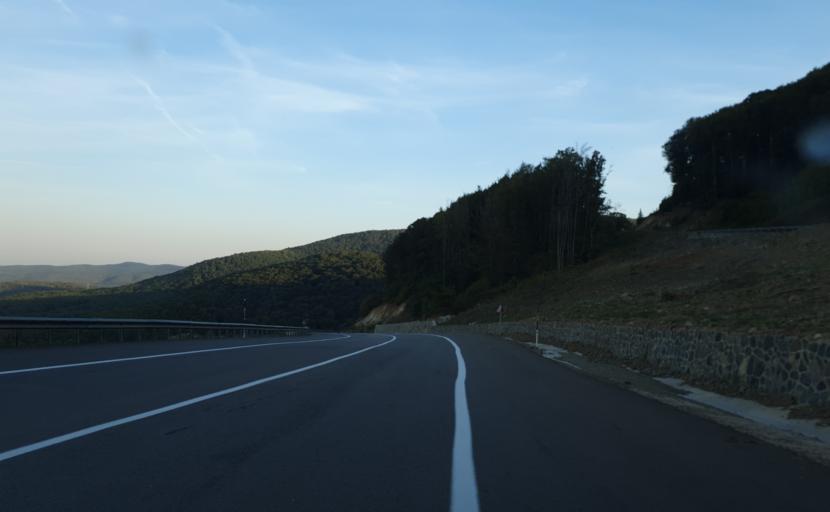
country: TR
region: Kirklareli
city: Sergen
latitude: 41.8147
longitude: 27.7454
